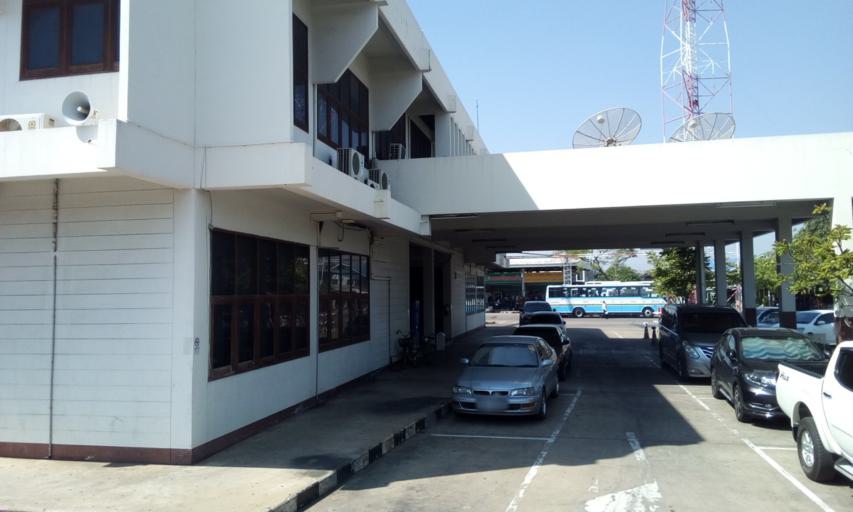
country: TH
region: Nakhon Ratchasima
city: Nakhon Ratchasima
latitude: 14.9898
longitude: 102.0949
